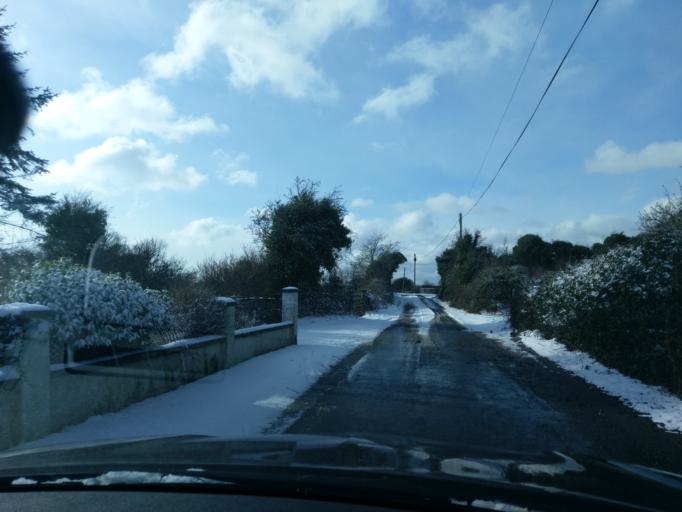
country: IE
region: Connaught
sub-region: County Galway
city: Athenry
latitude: 53.2145
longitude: -8.7603
